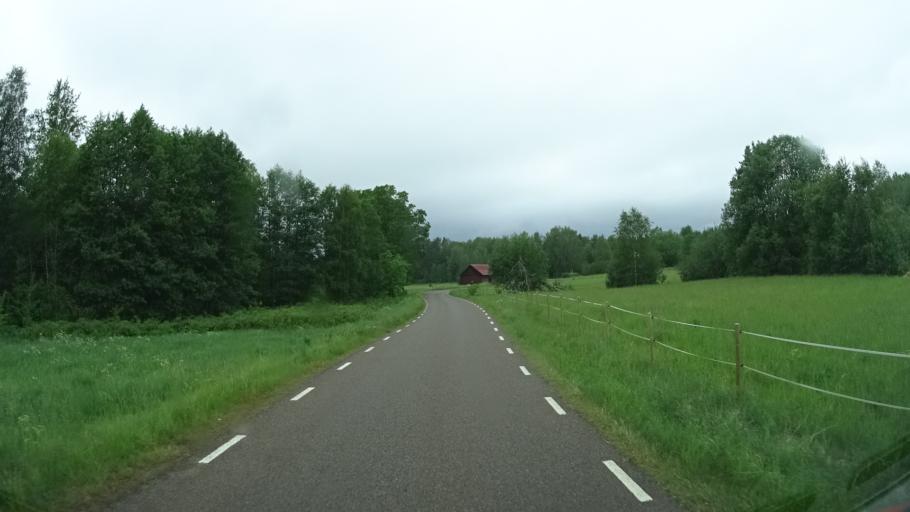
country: SE
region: Kalmar
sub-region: Vimmerby Kommun
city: Sodra Vi
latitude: 57.7028
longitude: 15.7443
